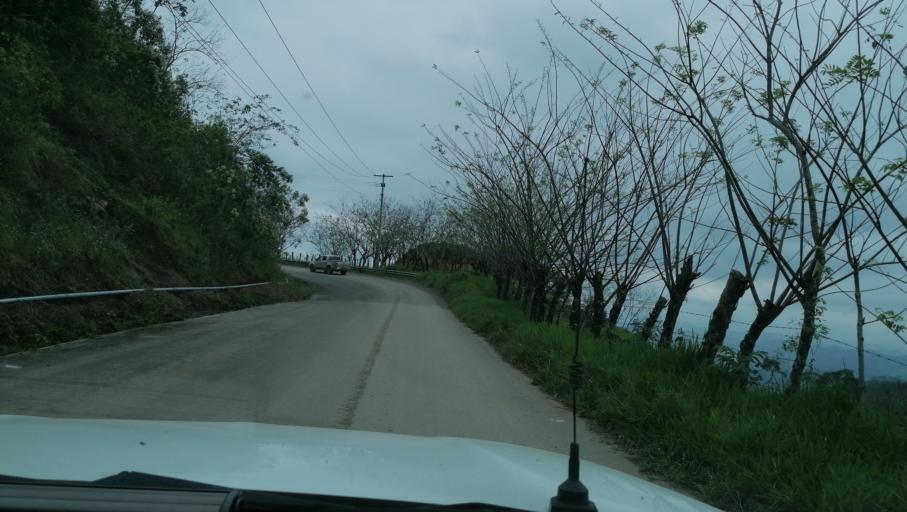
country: MX
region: Chiapas
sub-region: Francisco Leon
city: San Miguel la Sardina
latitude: 17.2717
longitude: -93.2662
